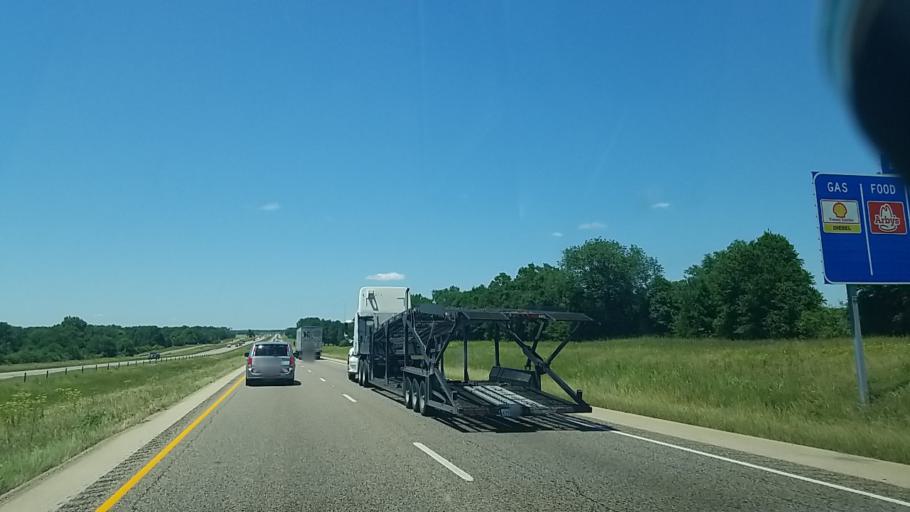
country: US
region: Texas
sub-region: Madison County
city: Madisonville
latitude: 31.0786
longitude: -95.9562
